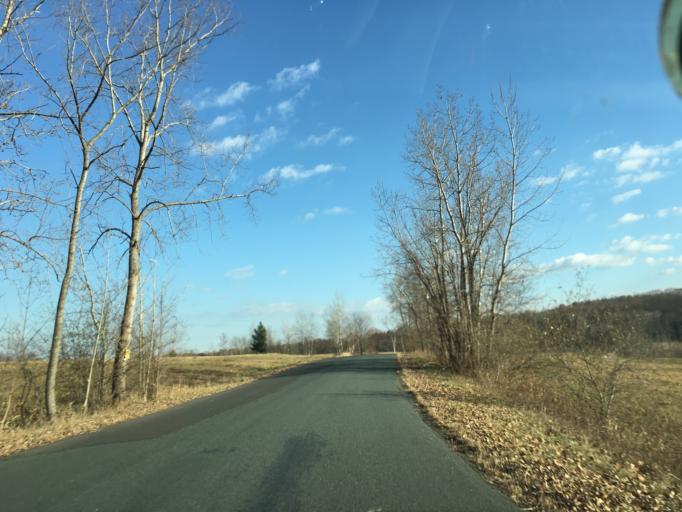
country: US
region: New York
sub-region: Rensselaer County
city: West Sand Lake
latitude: 42.6039
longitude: -73.5906
